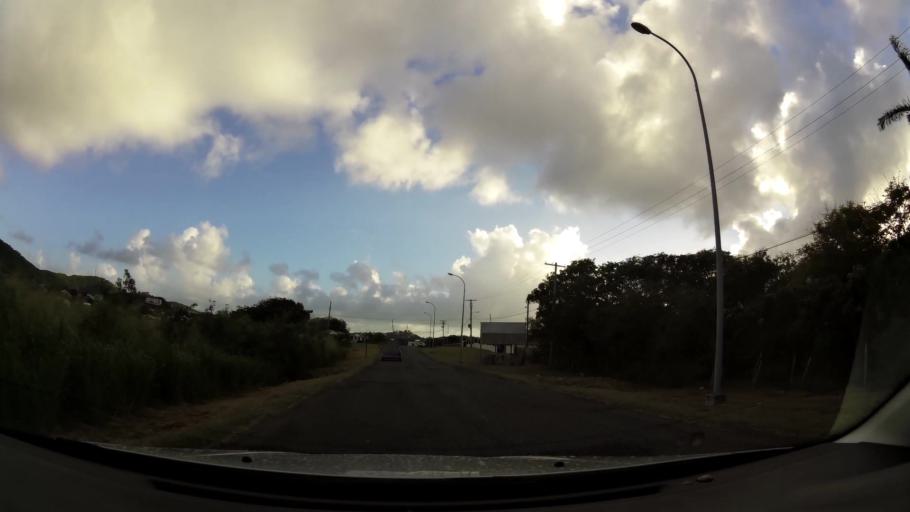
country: AG
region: Saint John
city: Saint John's
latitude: 17.1597
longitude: -61.8260
